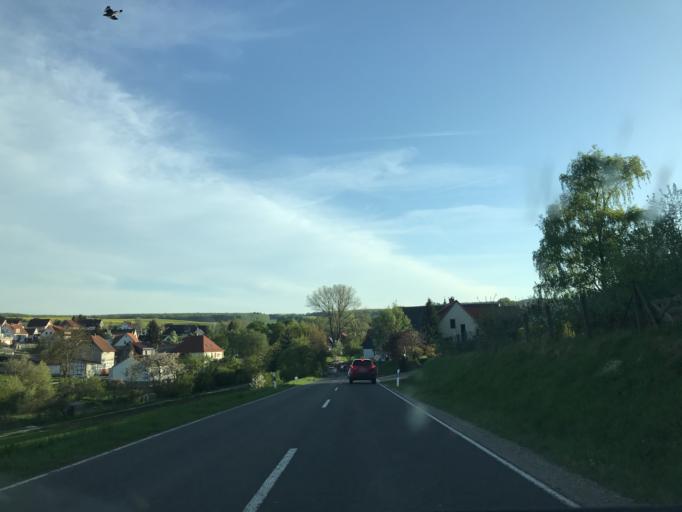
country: DE
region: Thuringia
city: Heuthen
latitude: 51.3362
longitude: 10.2272
